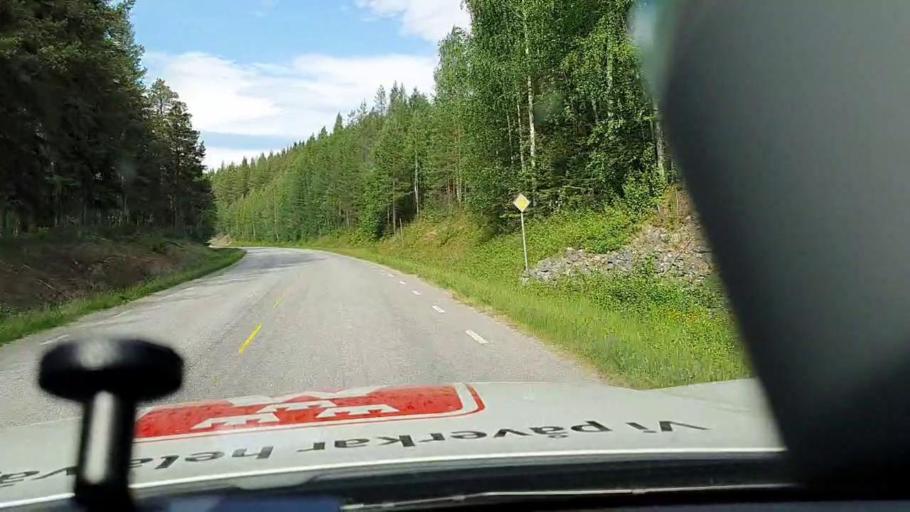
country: SE
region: Norrbotten
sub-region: Gallivare Kommun
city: Gaellivare
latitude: 66.4444
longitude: 20.6499
